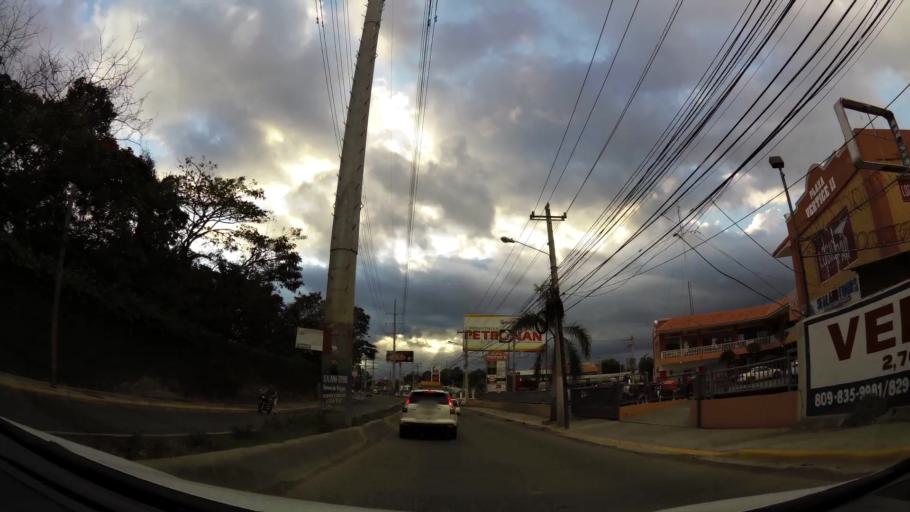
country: DO
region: Nacional
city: Santo Domingo
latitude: 18.5067
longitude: -69.9780
